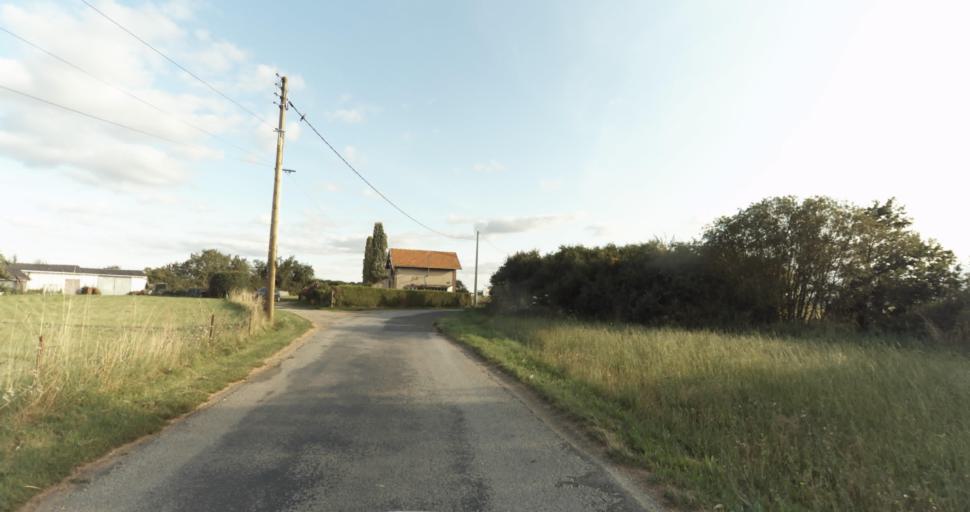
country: FR
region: Haute-Normandie
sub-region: Departement de l'Eure
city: Marcilly-sur-Eure
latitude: 48.8991
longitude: 1.2757
